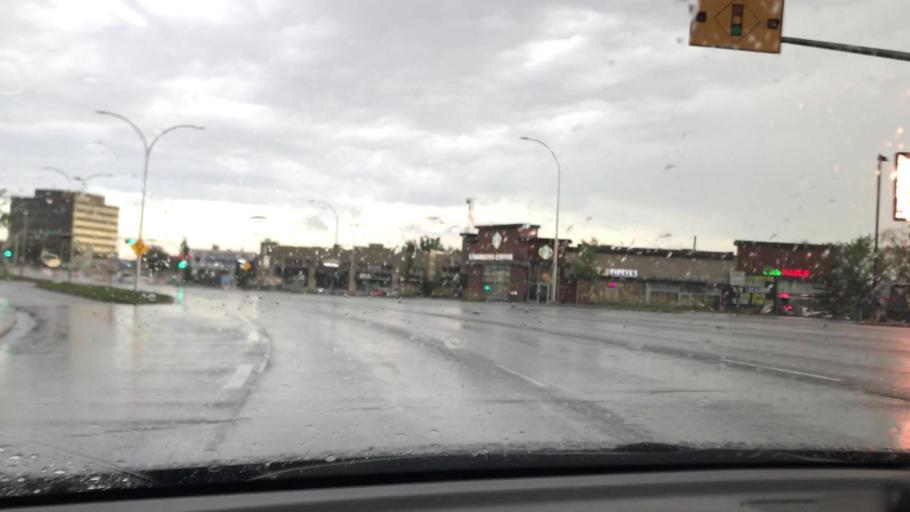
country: CA
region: Alberta
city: Edmonton
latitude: 53.4933
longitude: -113.4978
